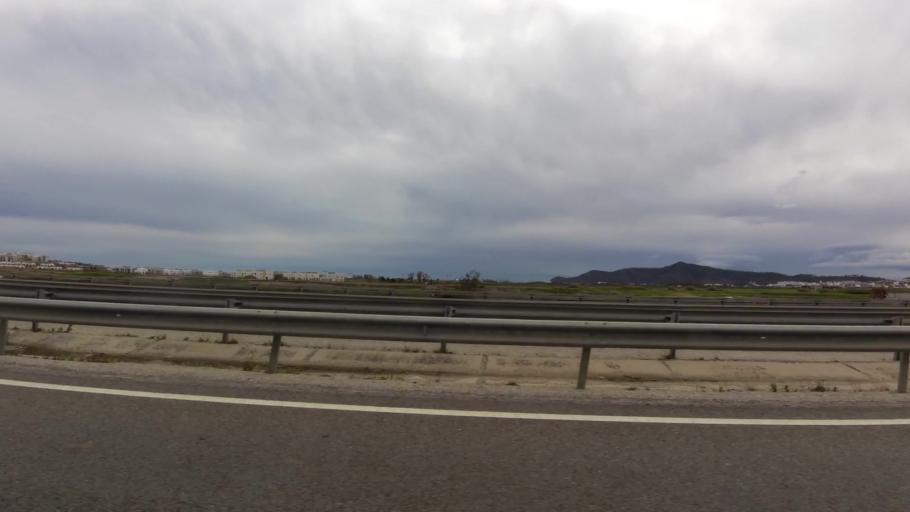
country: MA
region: Tanger-Tetouan
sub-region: Tetouan
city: Martil
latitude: 35.7136
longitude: -5.3553
